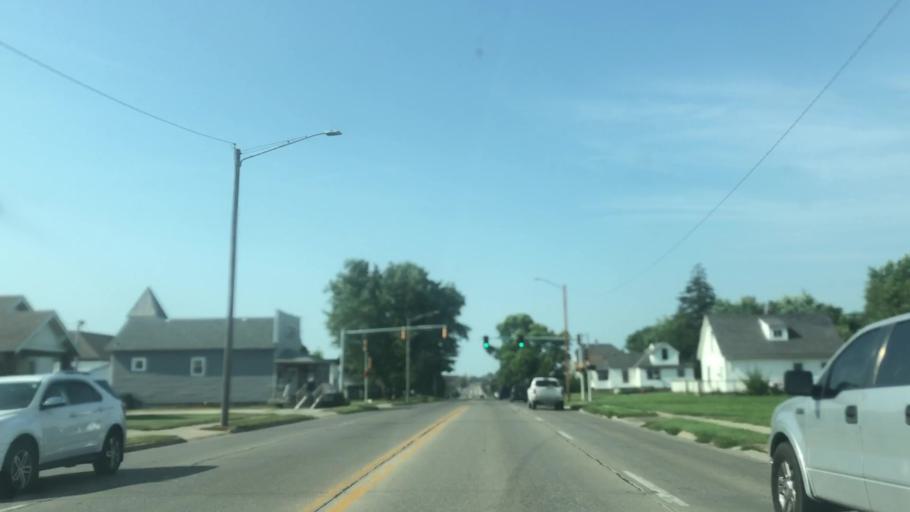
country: US
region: Iowa
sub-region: Marshall County
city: Marshalltown
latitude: 42.0339
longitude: -92.9127
